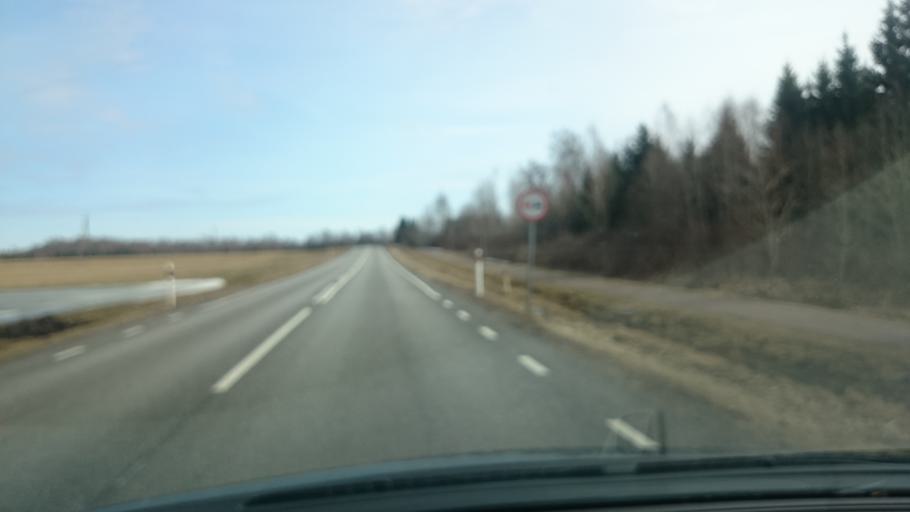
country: EE
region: Jaervamaa
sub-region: Paide linn
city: Paide
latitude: 58.8860
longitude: 25.5099
